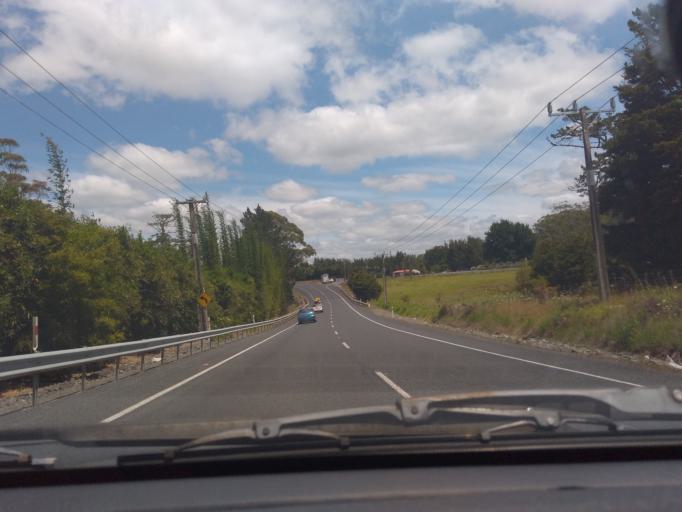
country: NZ
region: Northland
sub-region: Far North District
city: Kerikeri
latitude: -35.1877
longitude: 173.9103
